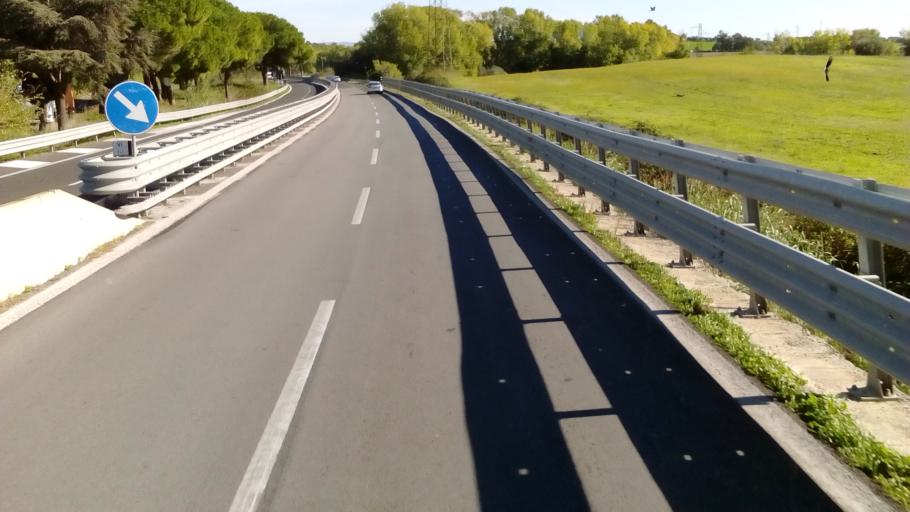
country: IT
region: Latium
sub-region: Provincia di Viterbo
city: Montalto di Castro
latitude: 42.3586
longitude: 11.5869
